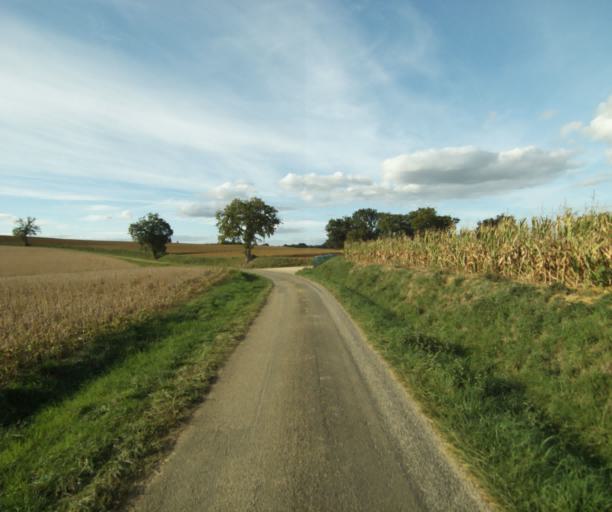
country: FR
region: Midi-Pyrenees
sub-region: Departement du Gers
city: Gondrin
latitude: 43.8923
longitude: 0.2804
